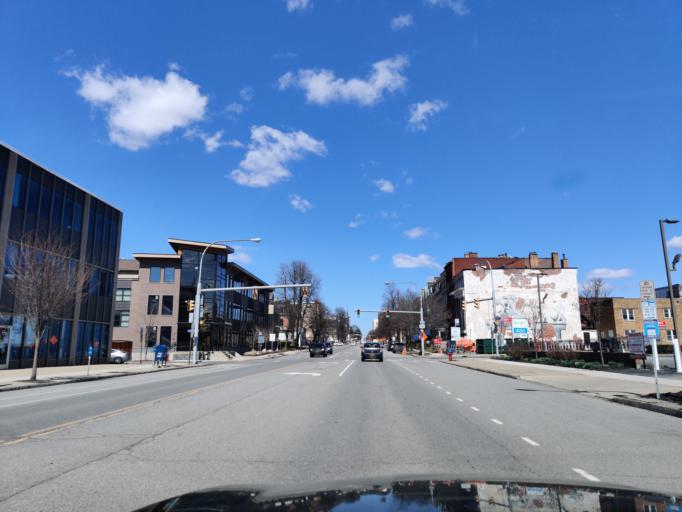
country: US
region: New York
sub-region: Erie County
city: Buffalo
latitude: 42.8963
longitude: -78.8749
